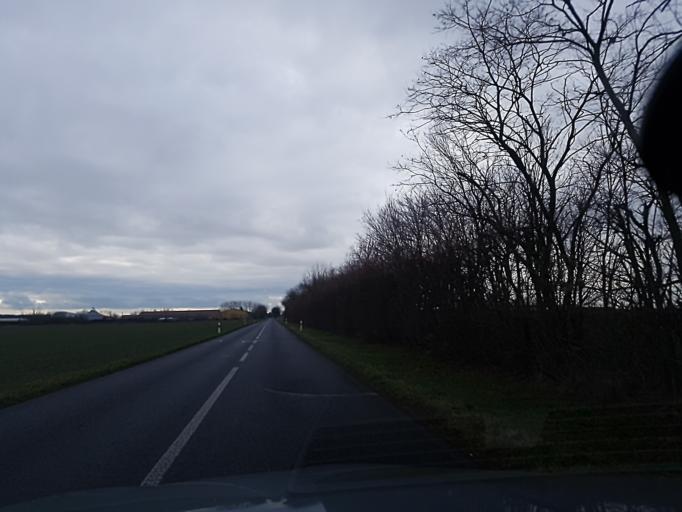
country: DE
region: Brandenburg
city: Falkenberg
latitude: 51.5368
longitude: 13.3113
